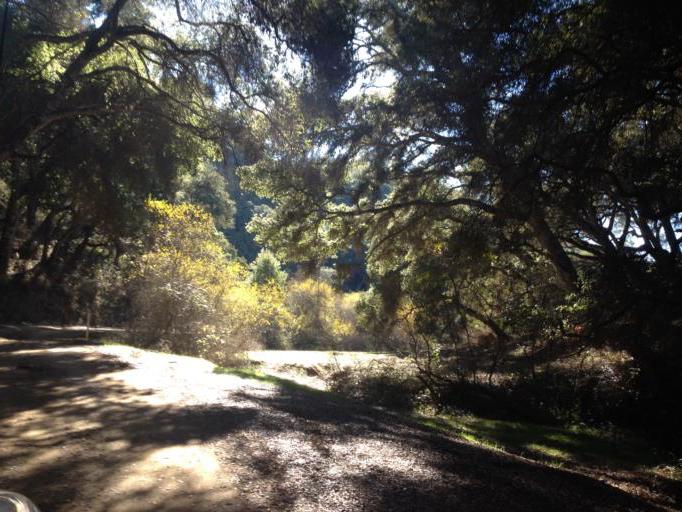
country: US
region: California
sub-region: San Luis Obispo County
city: Avila Beach
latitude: 35.2430
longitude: -120.7775
